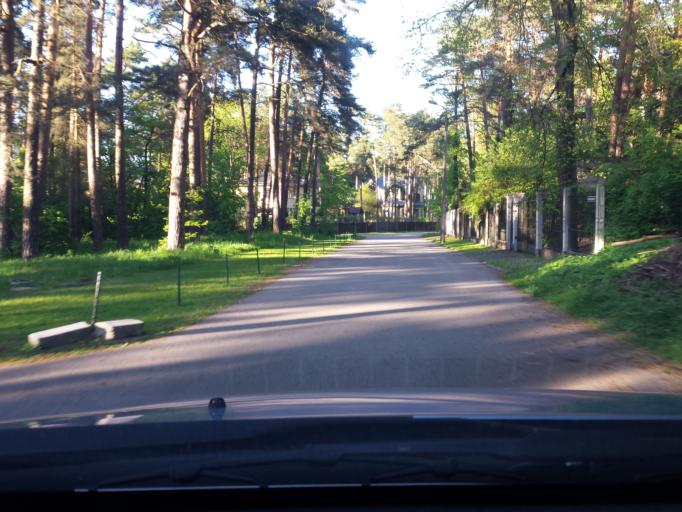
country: LV
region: Riga
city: Jaunciems
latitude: 57.0013
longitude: 24.1656
